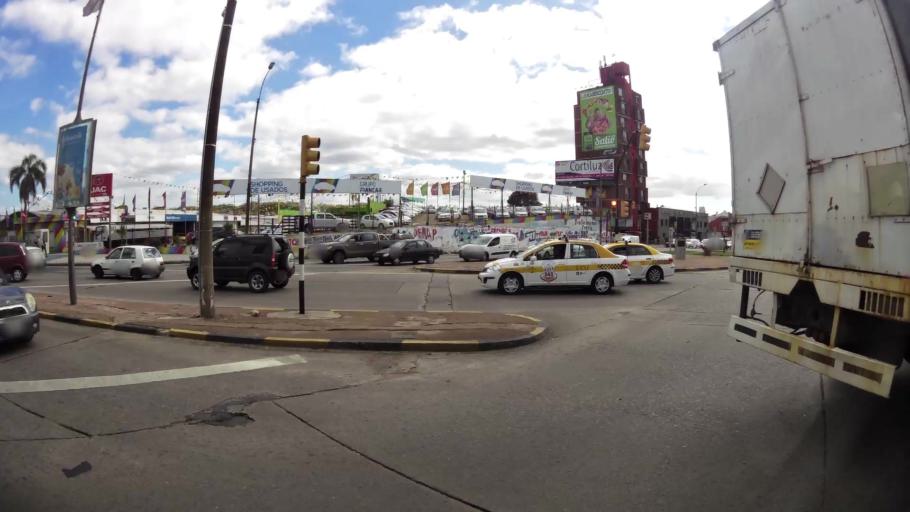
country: UY
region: Montevideo
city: Montevideo
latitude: -34.8867
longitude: -56.1378
